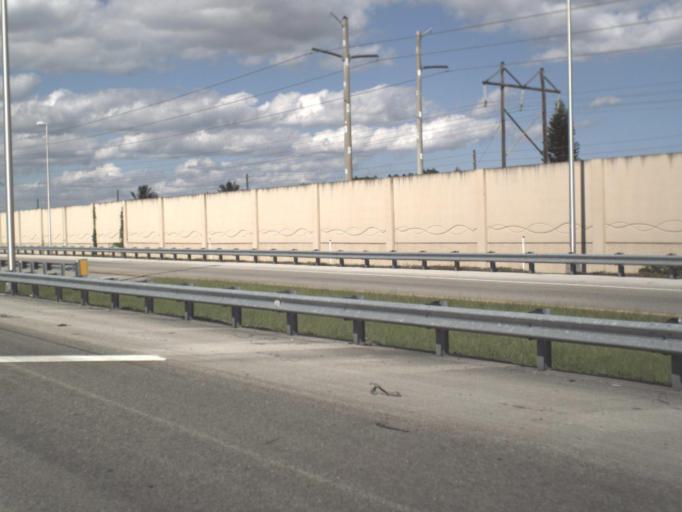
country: US
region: Florida
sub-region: Broward County
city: Lauderhill
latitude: 26.1316
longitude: -80.2181
